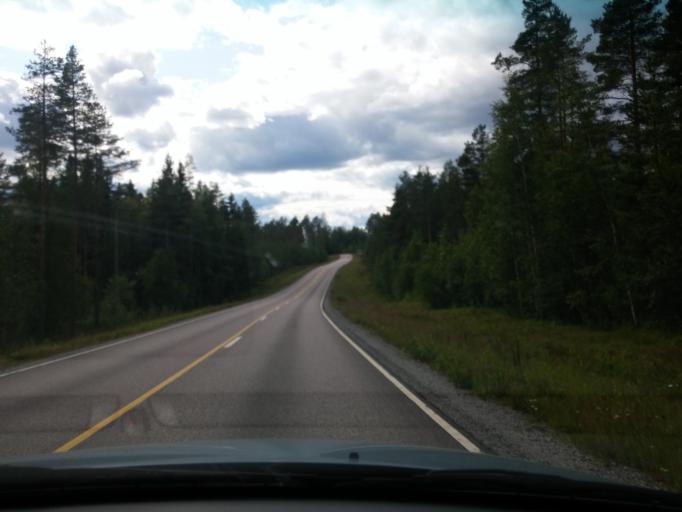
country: FI
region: Central Finland
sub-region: Saarijaervi-Viitasaari
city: Pylkoenmaeki
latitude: 62.6159
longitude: 24.7369
